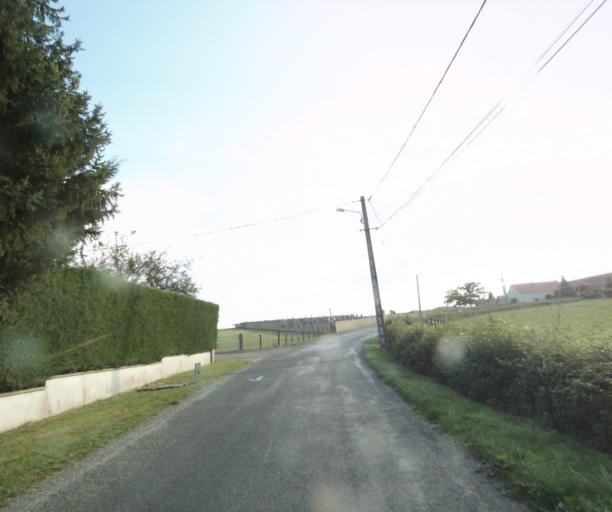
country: FR
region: Bourgogne
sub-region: Departement de Saone-et-Loire
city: Paray-le-Monial
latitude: 46.5296
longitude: 4.1225
